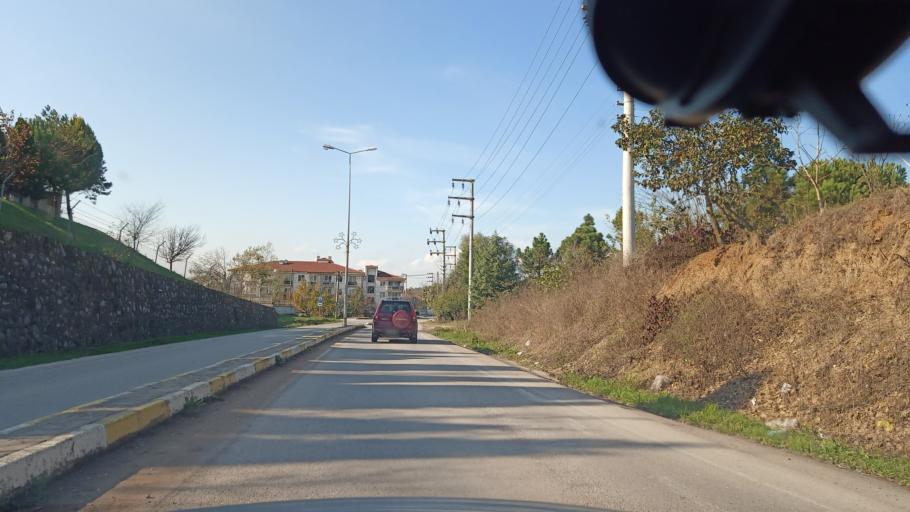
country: TR
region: Sakarya
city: Sogutlu
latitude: 40.8788
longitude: 30.4672
